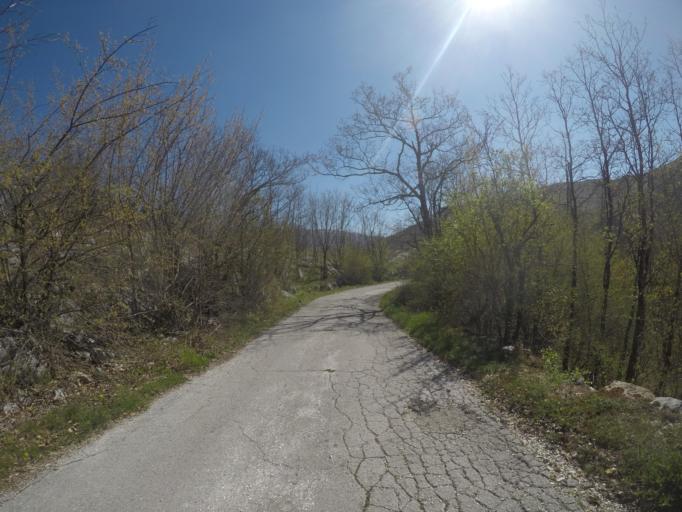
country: ME
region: Cetinje
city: Cetinje
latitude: 42.5373
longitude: 18.9840
